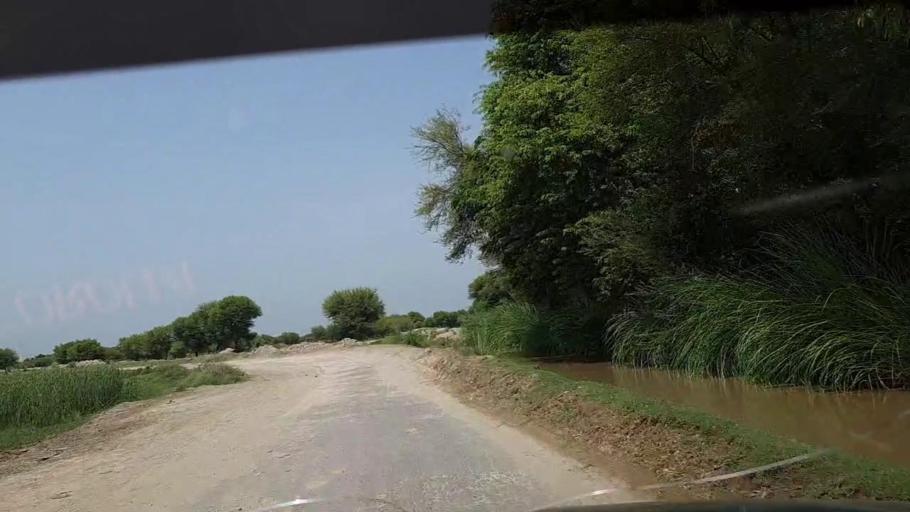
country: PK
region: Sindh
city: Khanpur
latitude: 27.8141
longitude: 69.4502
